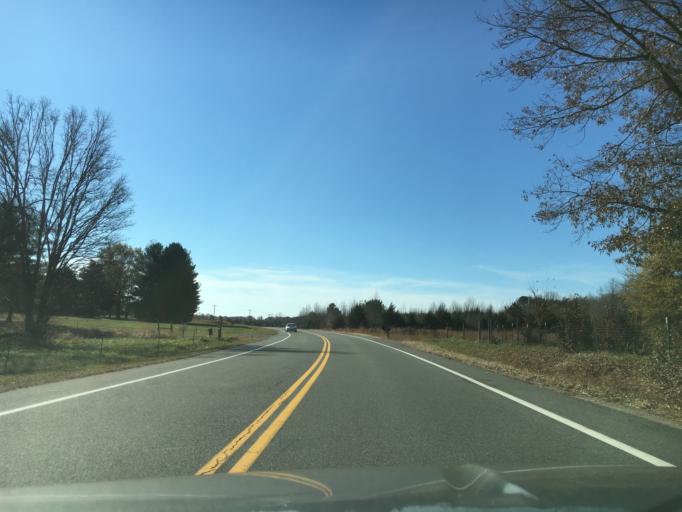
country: US
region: Virginia
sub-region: Cumberland County
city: Cumberland
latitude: 37.6105
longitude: -78.1596
